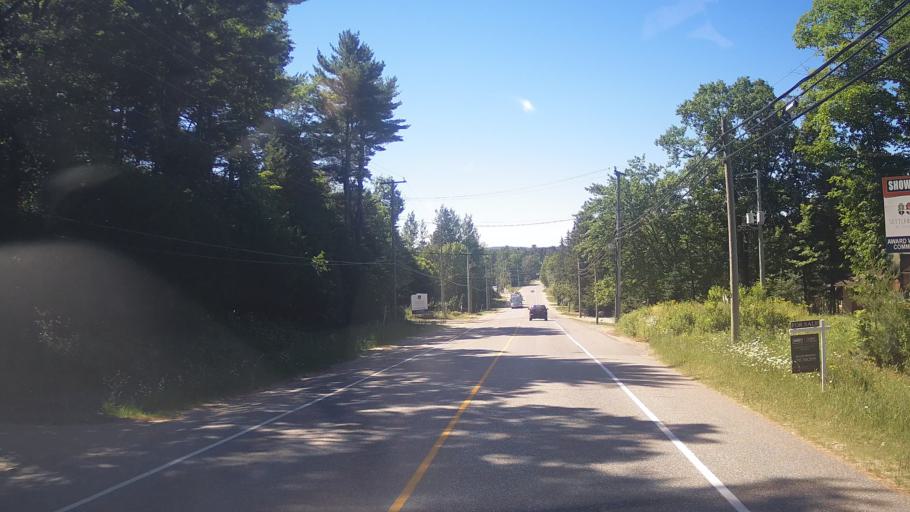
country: CA
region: Ontario
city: Huntsville
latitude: 45.3549
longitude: -79.2026
